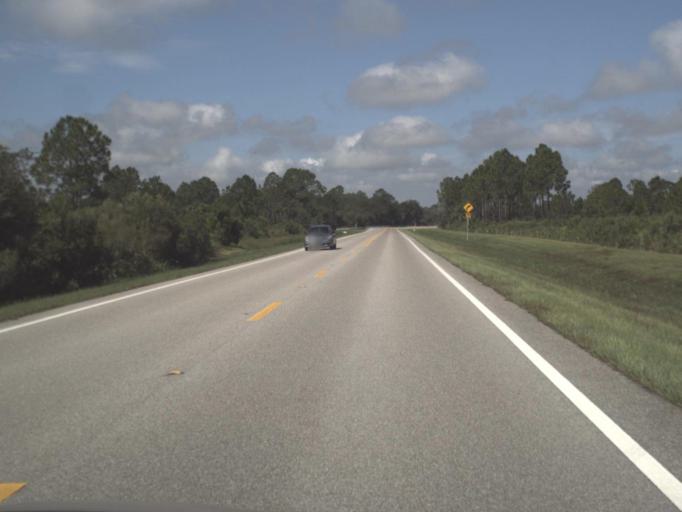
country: US
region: Florida
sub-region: Sarasota County
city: Lake Sarasota
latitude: 27.2222
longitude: -82.2940
